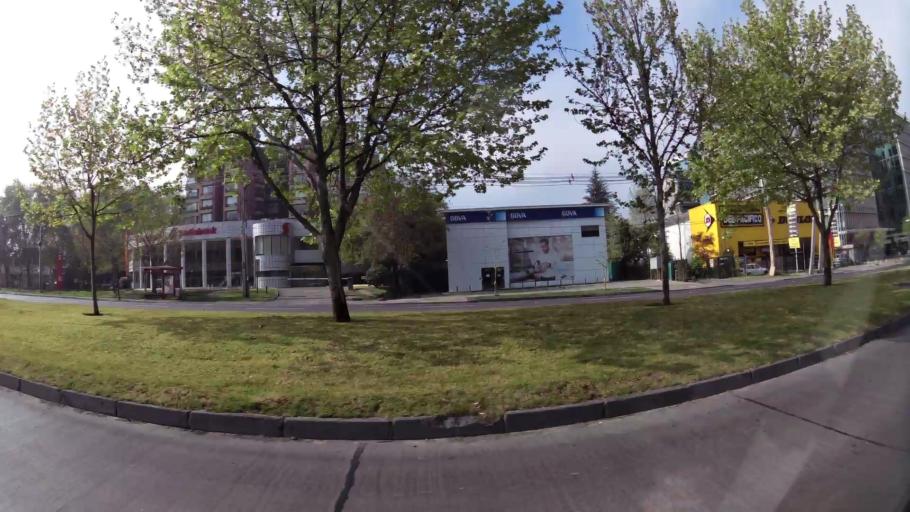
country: CL
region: Santiago Metropolitan
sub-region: Provincia de Santiago
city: Villa Presidente Frei, Nunoa, Santiago, Chile
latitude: -33.3766
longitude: -70.5264
